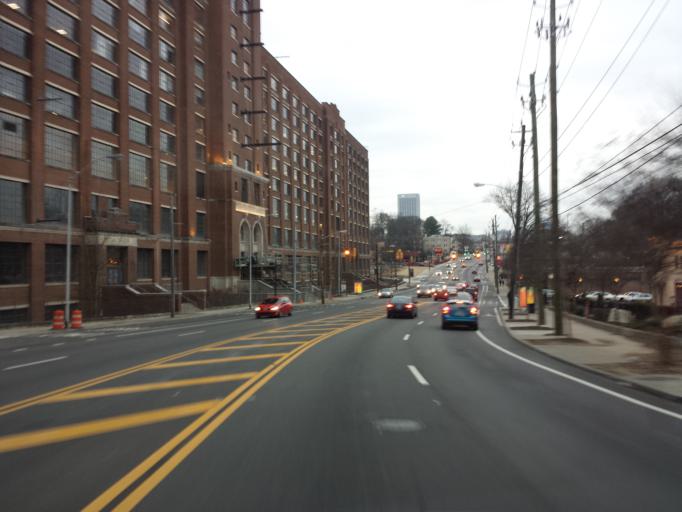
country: US
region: Georgia
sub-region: DeKalb County
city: Druid Hills
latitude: 33.7734
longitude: -84.3646
